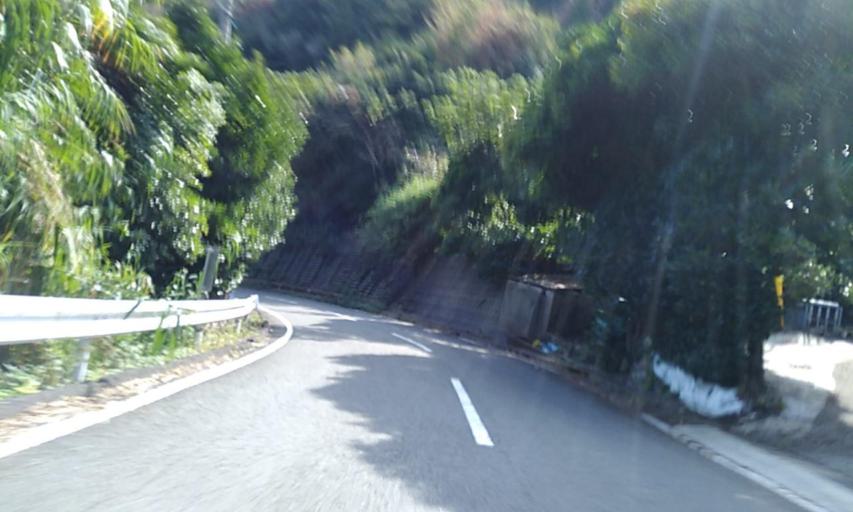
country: JP
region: Wakayama
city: Gobo
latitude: 33.9665
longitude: 135.0974
